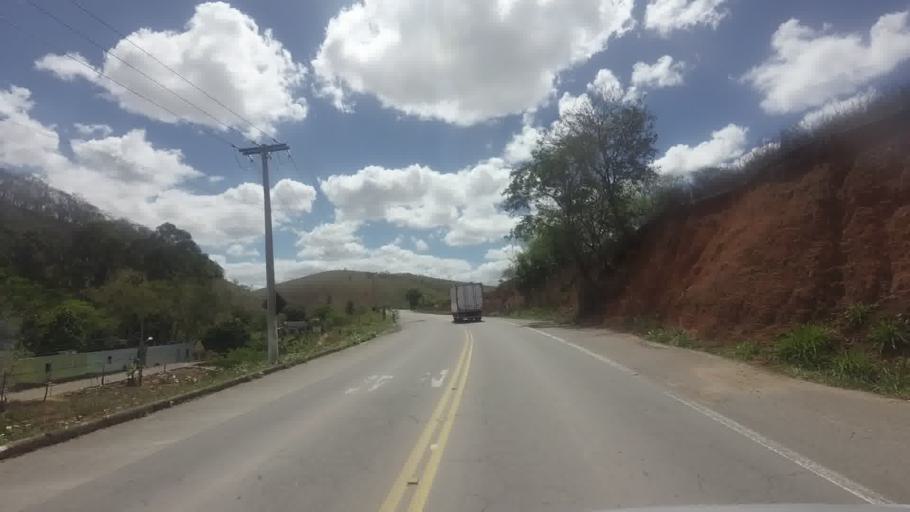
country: BR
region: Rio de Janeiro
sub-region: Santo Antonio De Padua
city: Santo Antonio de Padua
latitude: -21.6343
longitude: -42.2705
